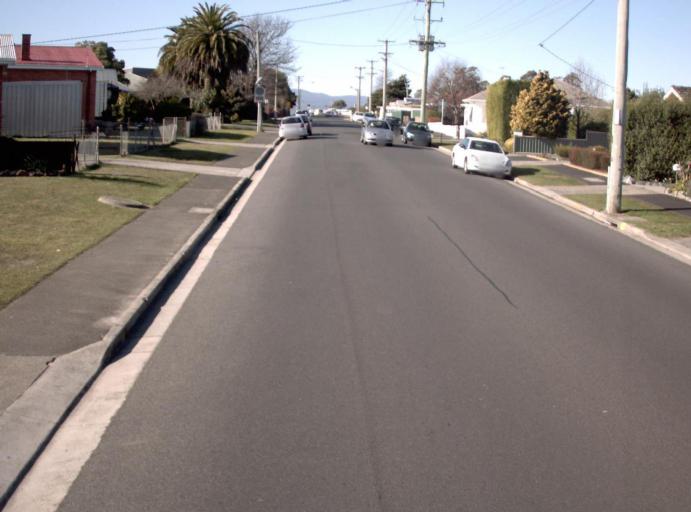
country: AU
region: Tasmania
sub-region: Launceston
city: Summerhill
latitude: -41.4742
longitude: 147.1248
